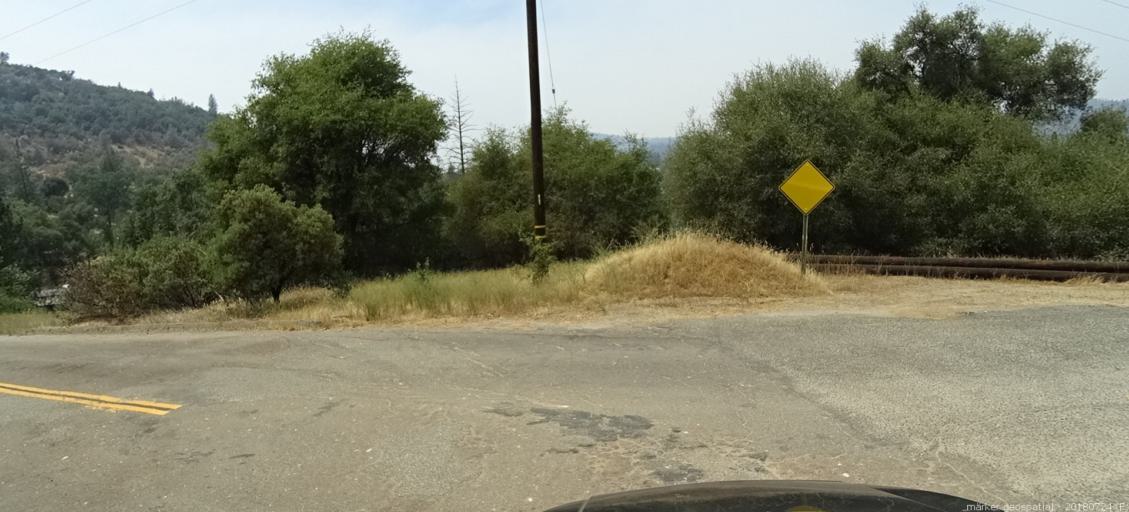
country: US
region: California
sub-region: Madera County
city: Oakhurst
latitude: 37.2456
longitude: -119.5579
